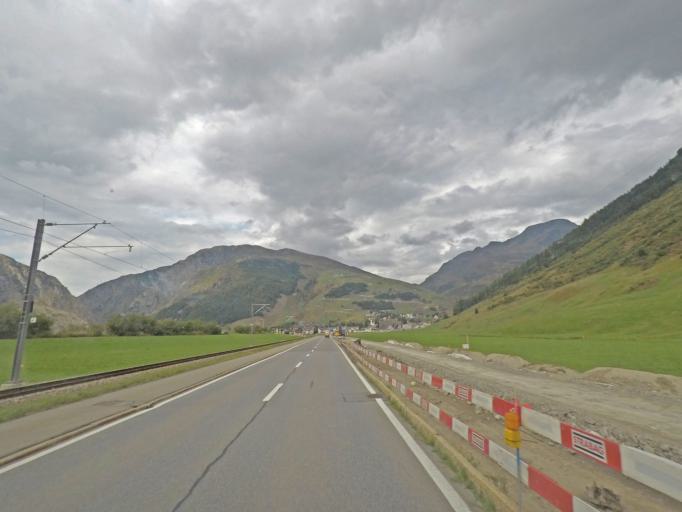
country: CH
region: Uri
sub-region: Uri
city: Andermatt
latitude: 46.6283
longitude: 8.5835
